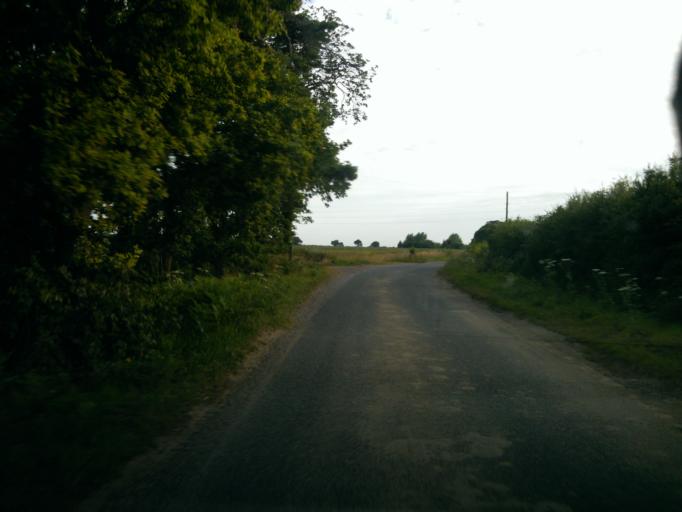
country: GB
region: England
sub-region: Essex
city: Great Bentley
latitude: 51.8361
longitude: 1.0820
